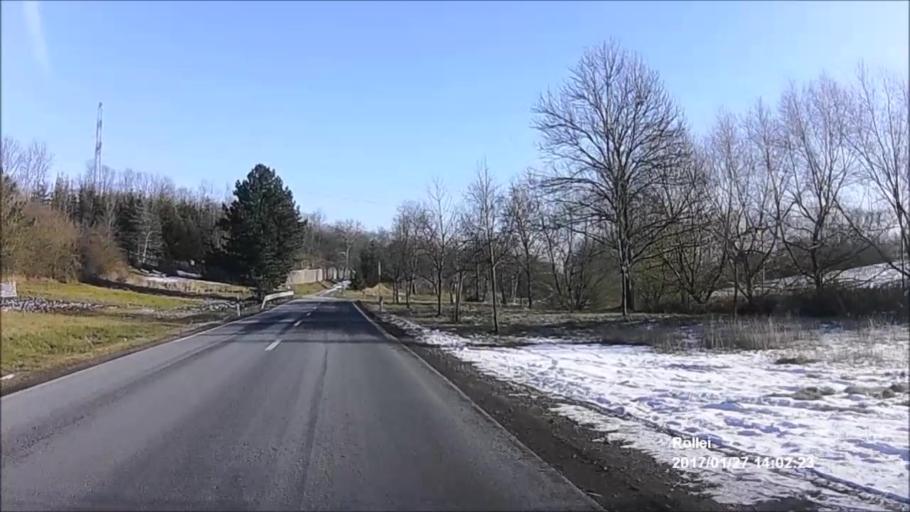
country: DE
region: Thuringia
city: Bruchstedt
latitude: 51.1835
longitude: 10.7908
